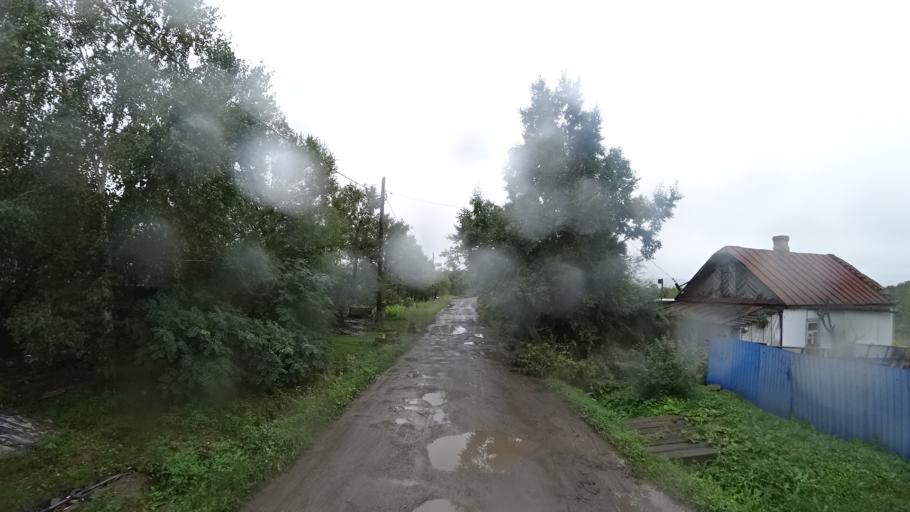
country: RU
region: Primorskiy
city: Monastyrishche
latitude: 44.2005
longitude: 132.4216
